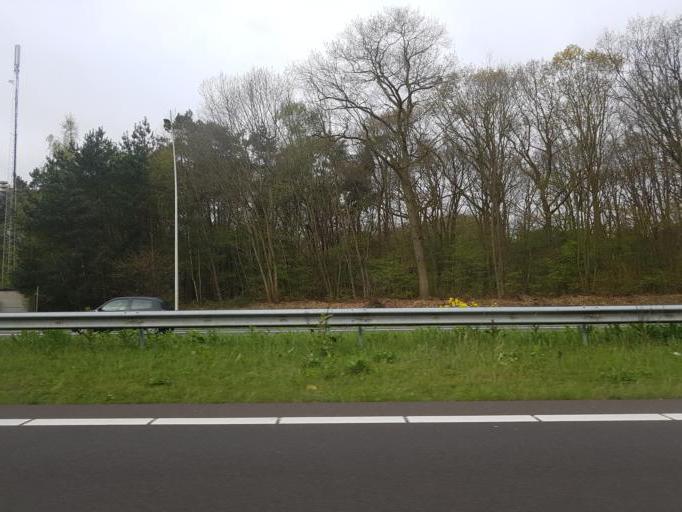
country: NL
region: North Brabant
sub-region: Gemeente Loon op Zand
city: Loon op Zand
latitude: 51.6429
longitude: 5.0593
